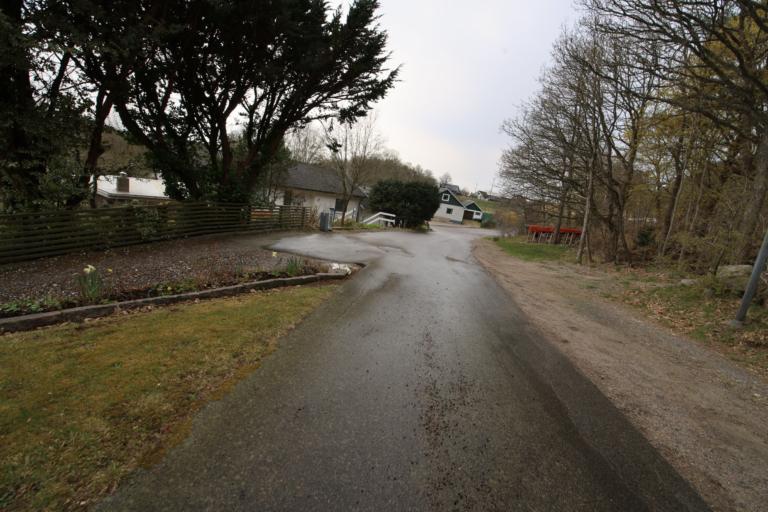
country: SE
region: Halland
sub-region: Varbergs Kommun
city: Tvaaker
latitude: 57.1492
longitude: 12.4606
